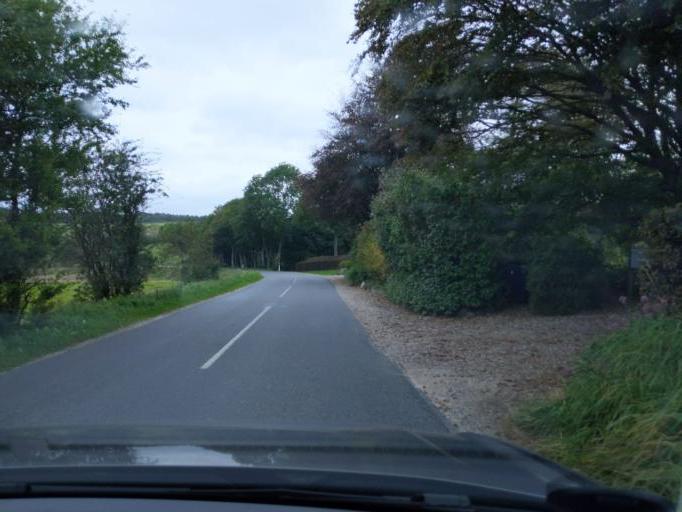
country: DK
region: North Denmark
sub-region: Mariagerfjord Kommune
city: Hobro
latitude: 56.5602
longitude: 9.7164
